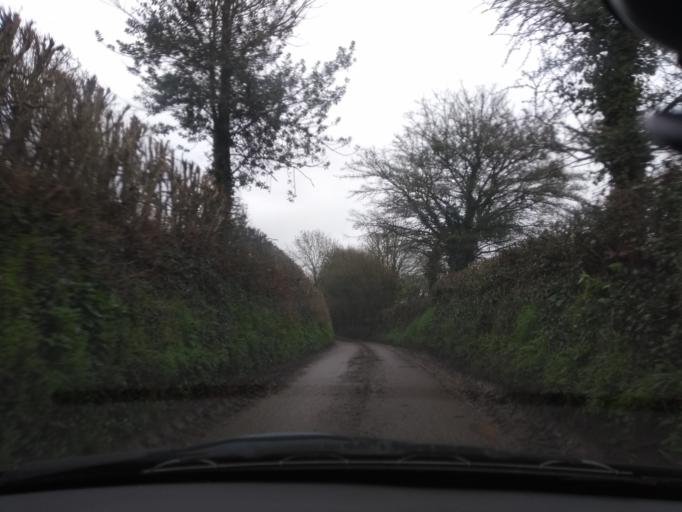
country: GB
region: England
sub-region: Somerset
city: Taunton
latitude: 51.0412
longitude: -3.1292
